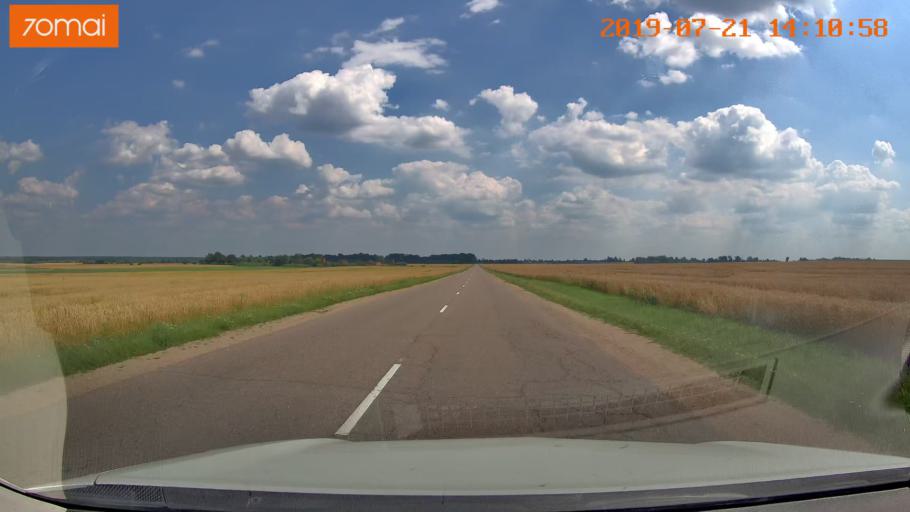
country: BY
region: Grodnenskaya
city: Karelichy
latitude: 53.6609
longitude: 26.1423
